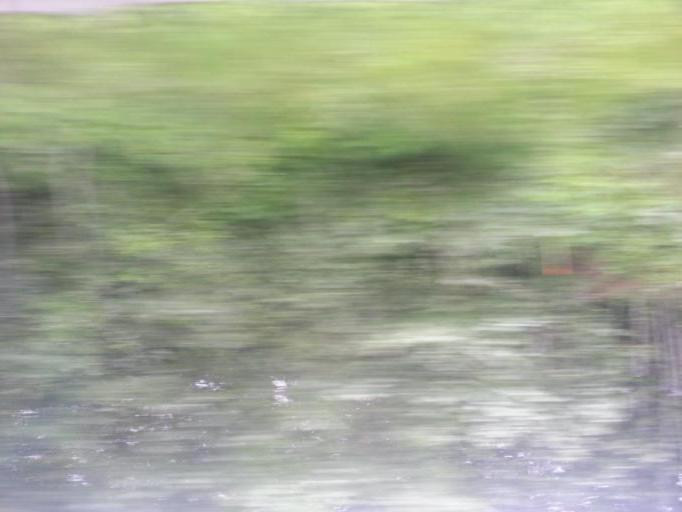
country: NO
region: Sor-Trondelag
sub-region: Malvik
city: Malvik
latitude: 63.4229
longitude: 10.5805
